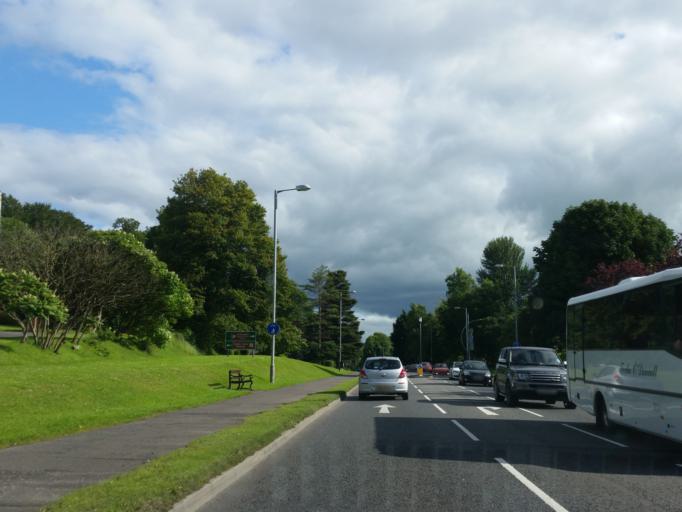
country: GB
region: Northern Ireland
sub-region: Fermanagh District
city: Enniskillen
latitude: 54.3391
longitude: -7.6254
